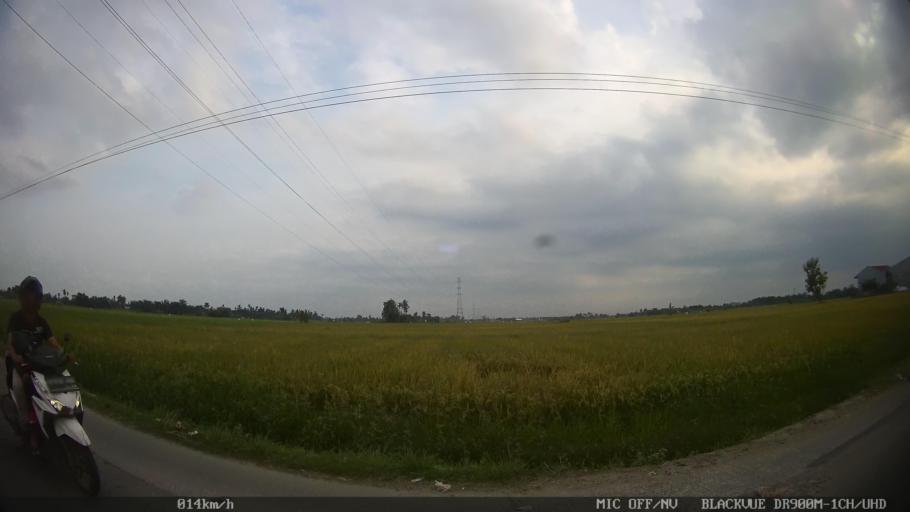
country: ID
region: North Sumatra
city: Sunggal
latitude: 3.5605
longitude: 98.5908
